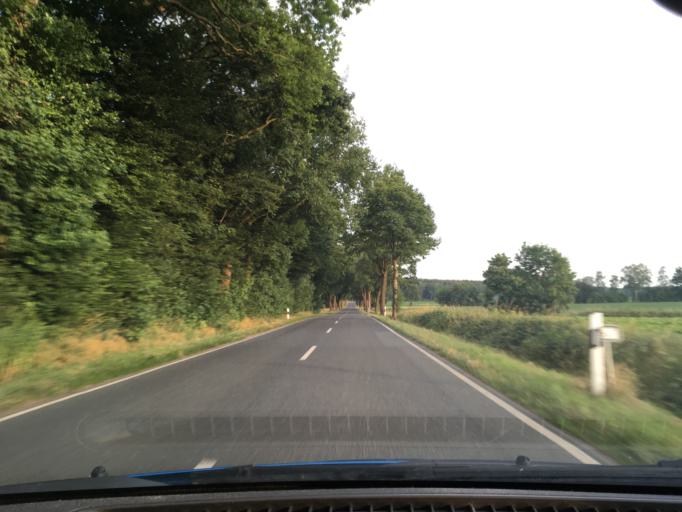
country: DE
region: Lower Saxony
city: Scharnhorst
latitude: 52.7146
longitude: 10.3175
